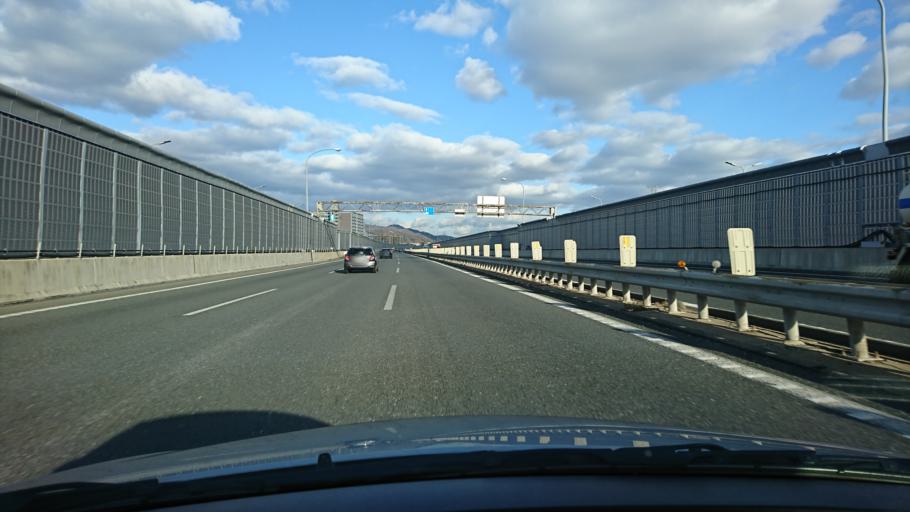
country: JP
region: Hyogo
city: Takarazuka
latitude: 34.8069
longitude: 135.3800
